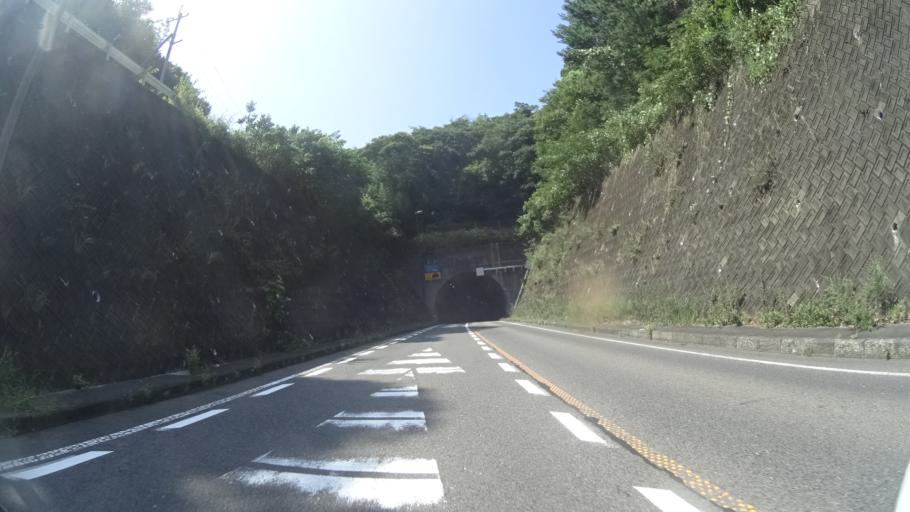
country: JP
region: Shimane
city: Masuda
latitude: 34.6658
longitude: 131.6891
